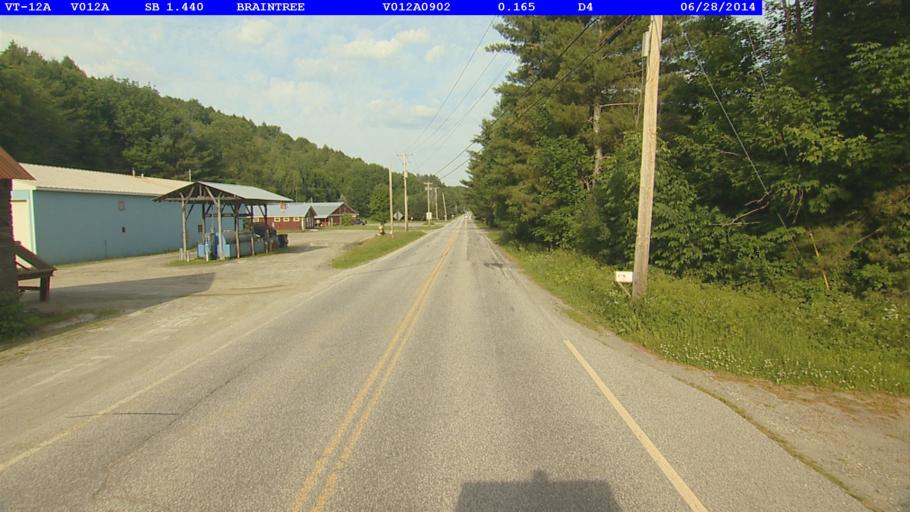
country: US
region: Vermont
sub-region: Orange County
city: Randolph
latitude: 43.9312
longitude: -72.6908
